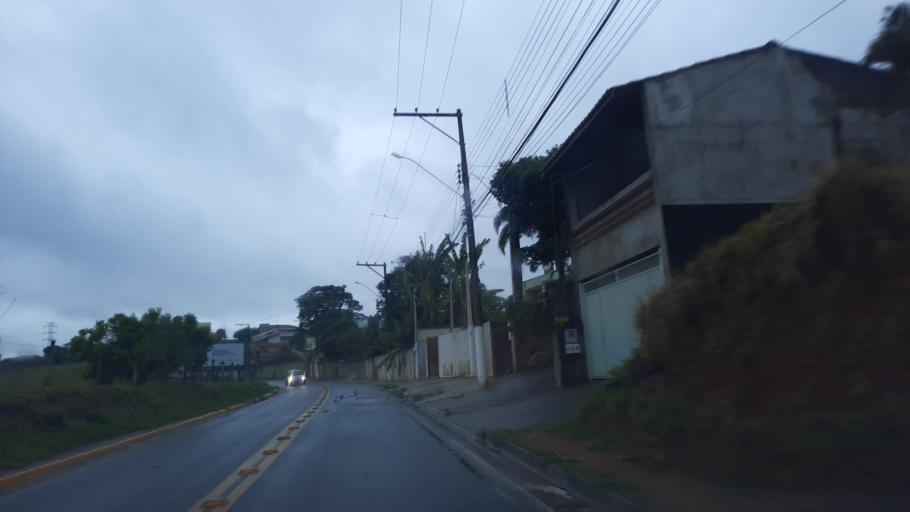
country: BR
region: Sao Paulo
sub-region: Atibaia
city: Atibaia
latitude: -23.0934
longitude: -46.5428
